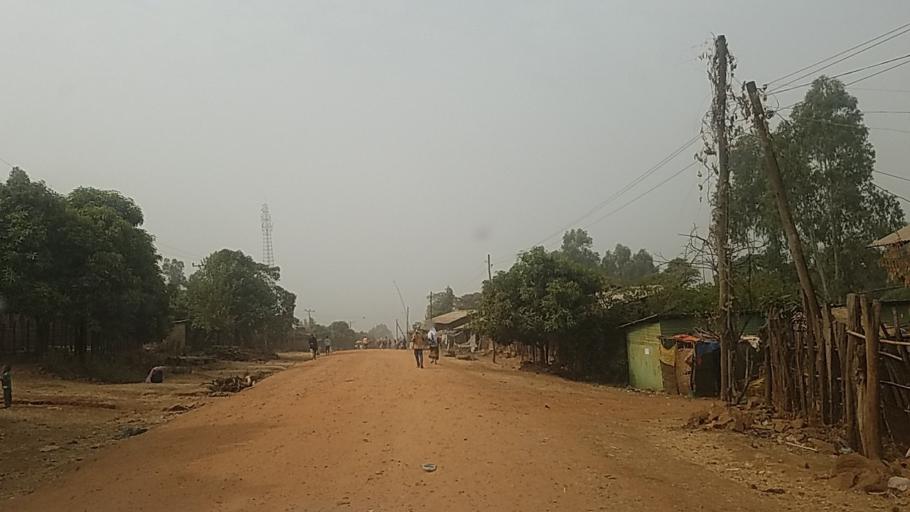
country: ET
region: Amhara
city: Bure
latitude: 10.8517
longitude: 36.3495
